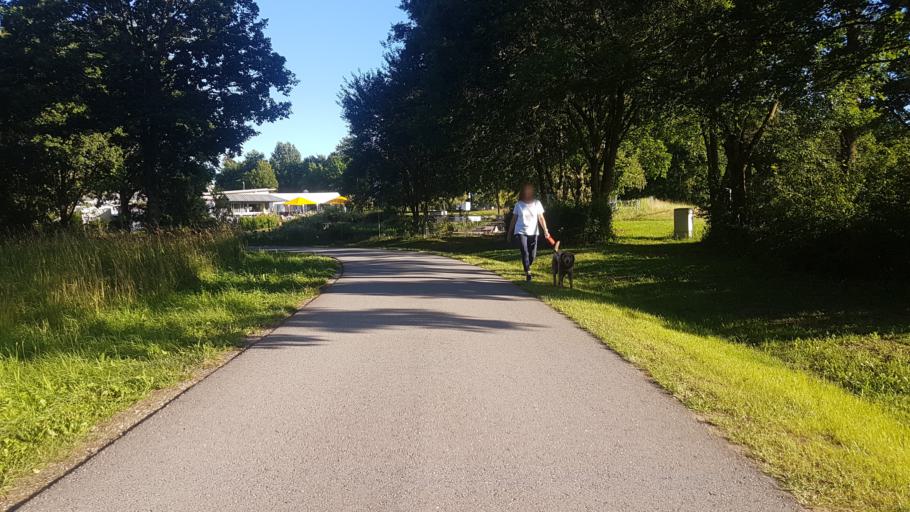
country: DE
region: Bavaria
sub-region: Regierungsbezirk Mittelfranken
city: Absberg
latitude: 49.1399
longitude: 10.8723
